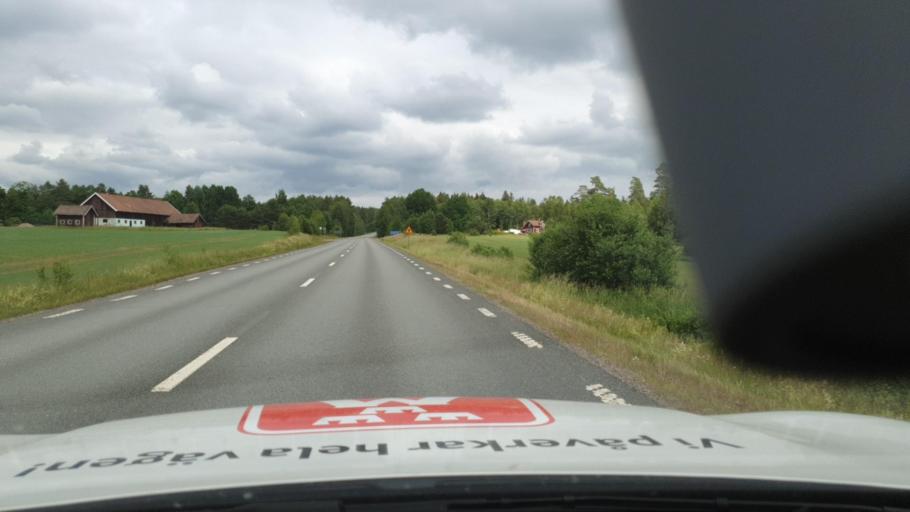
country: SE
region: Vaestra Goetaland
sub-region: Tidaholms Kommun
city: Olofstorp
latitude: 58.2204
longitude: 14.1045
